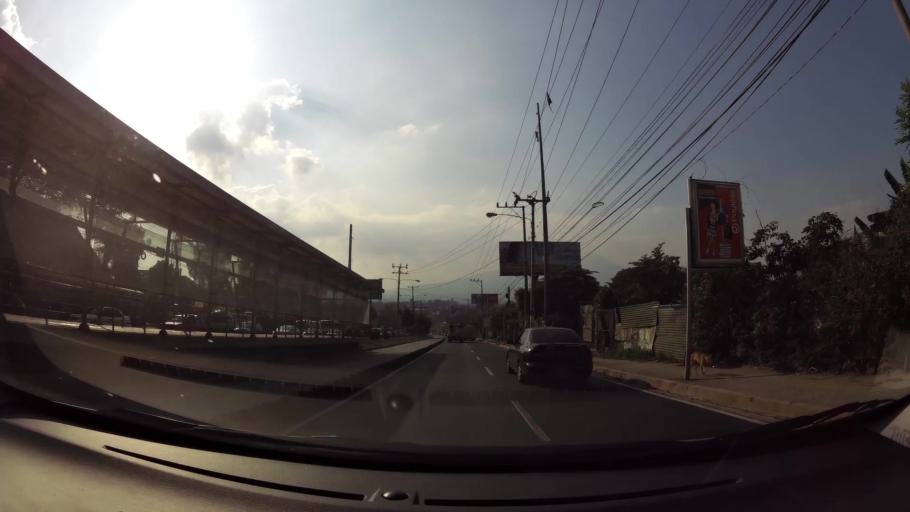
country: SV
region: San Salvador
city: Soyapango
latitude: 13.7011
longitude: -89.1568
